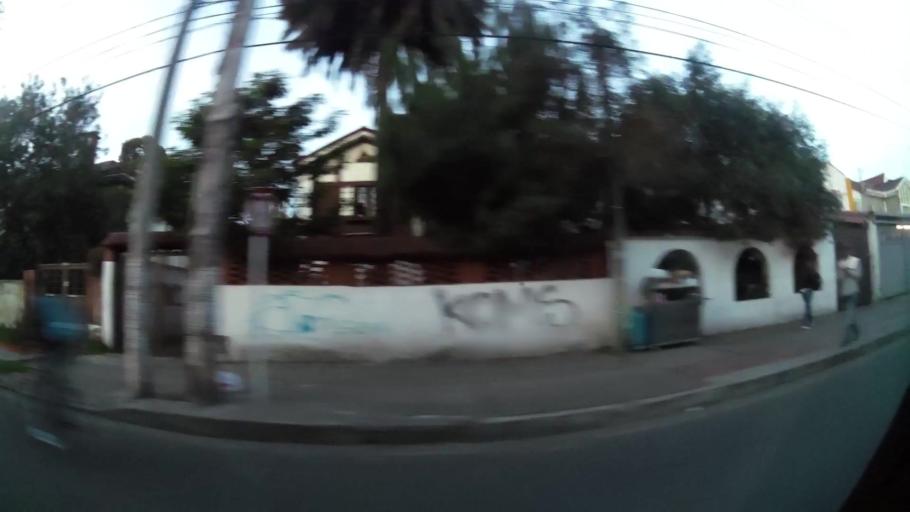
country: CO
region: Bogota D.C.
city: Barrio San Luis
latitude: 4.6552
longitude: -74.0653
